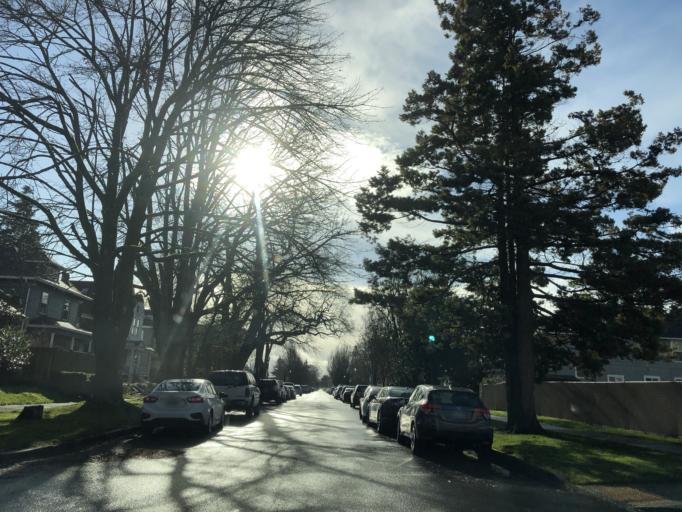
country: US
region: Washington
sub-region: Pierce County
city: Tacoma
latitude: 47.2590
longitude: -122.4562
